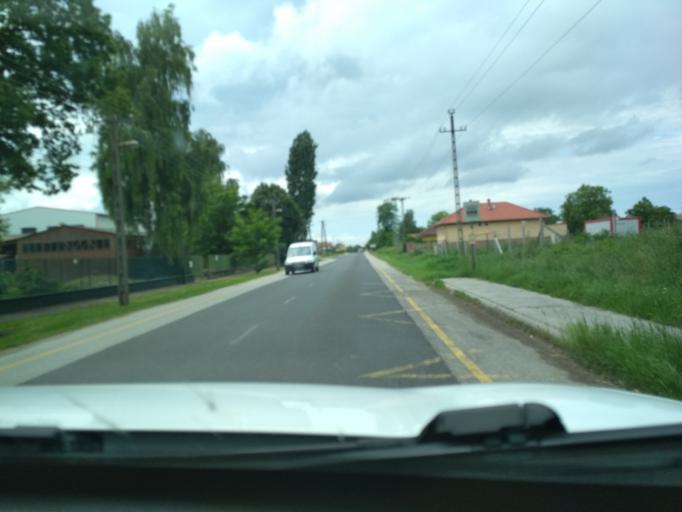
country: HU
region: Jasz-Nagykun-Szolnok
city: Tiszafured
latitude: 47.6123
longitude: 20.7324
